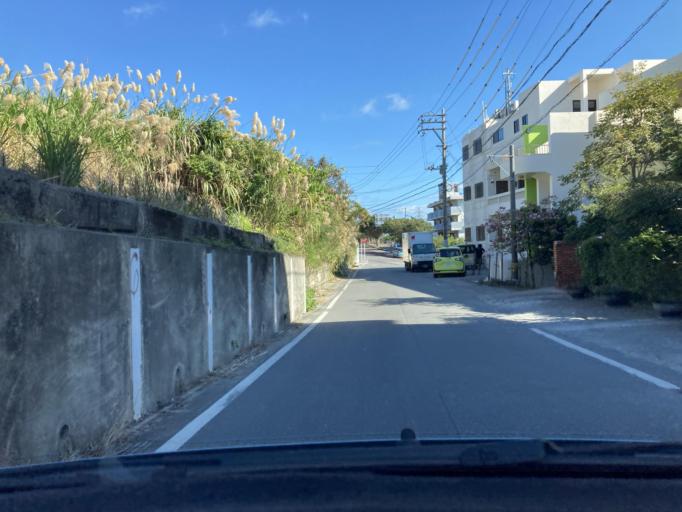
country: JP
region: Okinawa
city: Gushikawa
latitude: 26.3521
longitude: 127.8390
